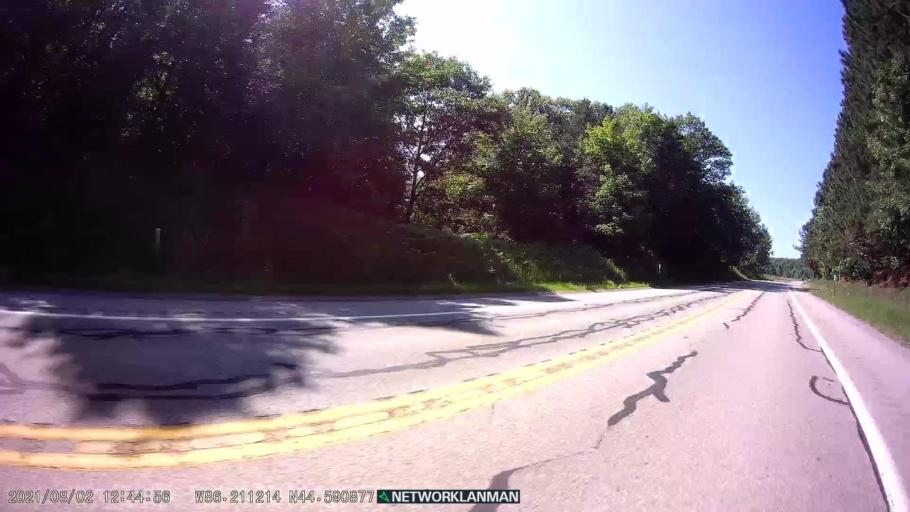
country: US
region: Michigan
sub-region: Benzie County
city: Frankfort
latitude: 44.5913
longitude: -86.2113
